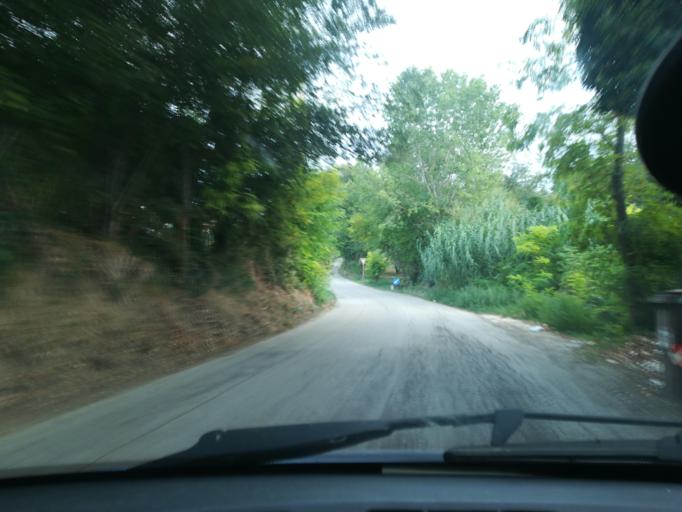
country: IT
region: The Marches
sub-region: Provincia di Macerata
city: Piediripa
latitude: 43.2980
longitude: 13.4814
